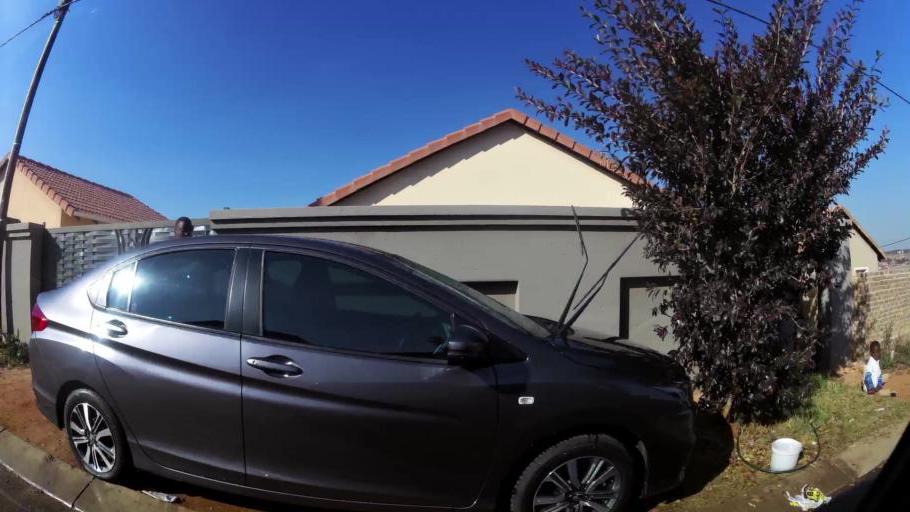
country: ZA
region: Gauteng
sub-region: West Rand District Municipality
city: Muldersdriseloop
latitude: -26.0355
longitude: 27.9140
